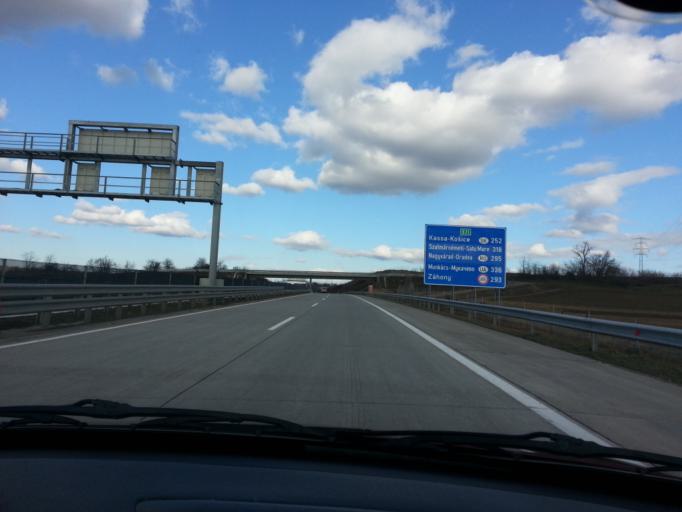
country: HU
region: Pest
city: Nagytarcsa
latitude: 47.5182
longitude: 19.3017
